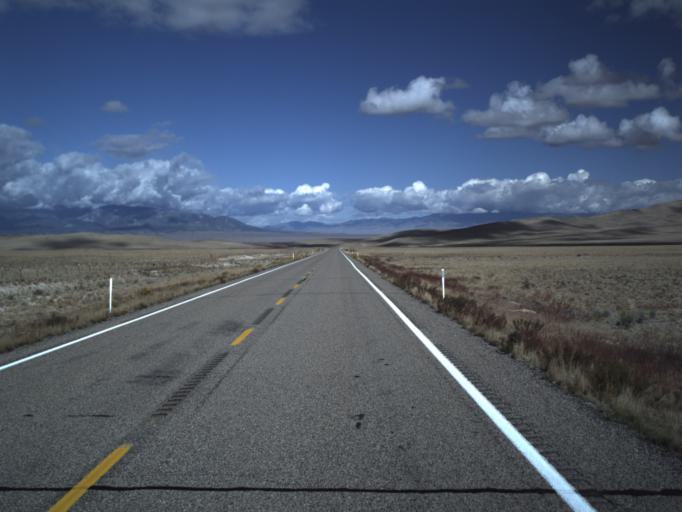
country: US
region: Nevada
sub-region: Lincoln County
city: Pioche
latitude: 38.7008
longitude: -113.9078
